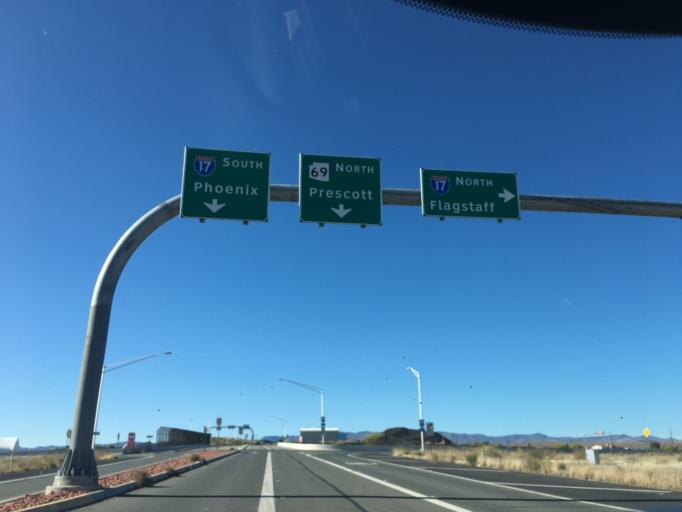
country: US
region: Arizona
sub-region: Yavapai County
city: Cordes Lakes
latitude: 34.3336
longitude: -112.1183
